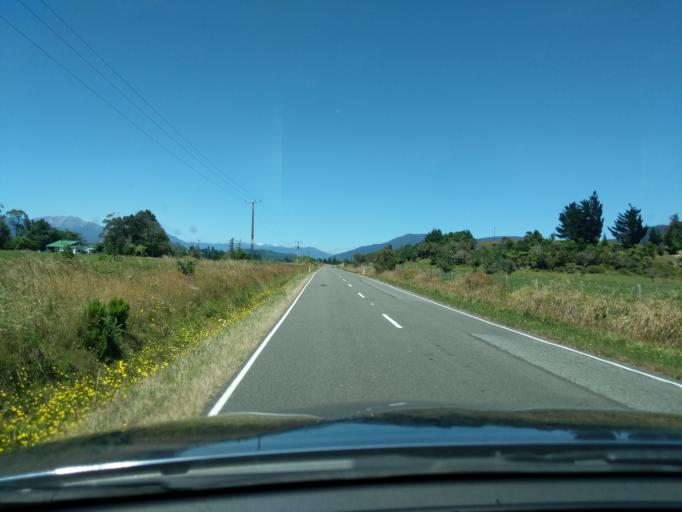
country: NZ
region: Tasman
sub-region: Tasman District
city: Takaka
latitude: -40.6882
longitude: 172.6474
